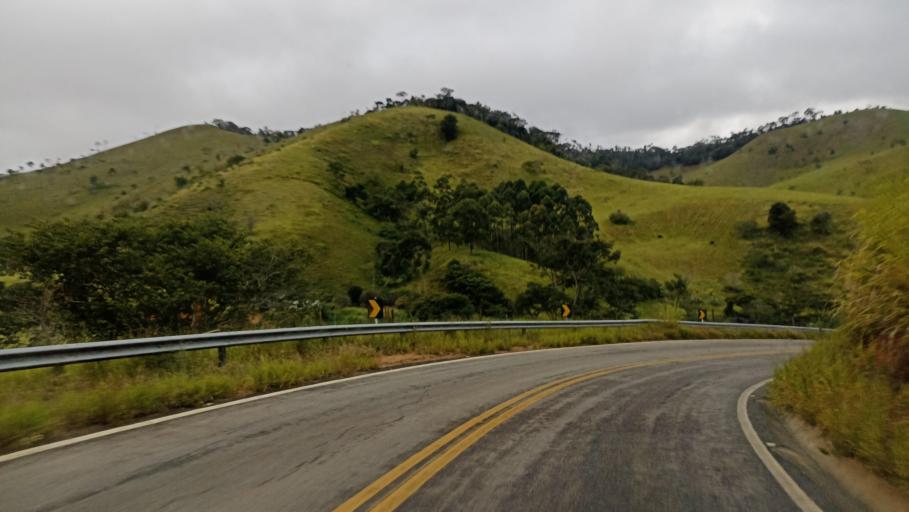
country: BR
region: Bahia
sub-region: Itanhem
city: Itanhem
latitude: -16.6905
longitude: -40.5104
